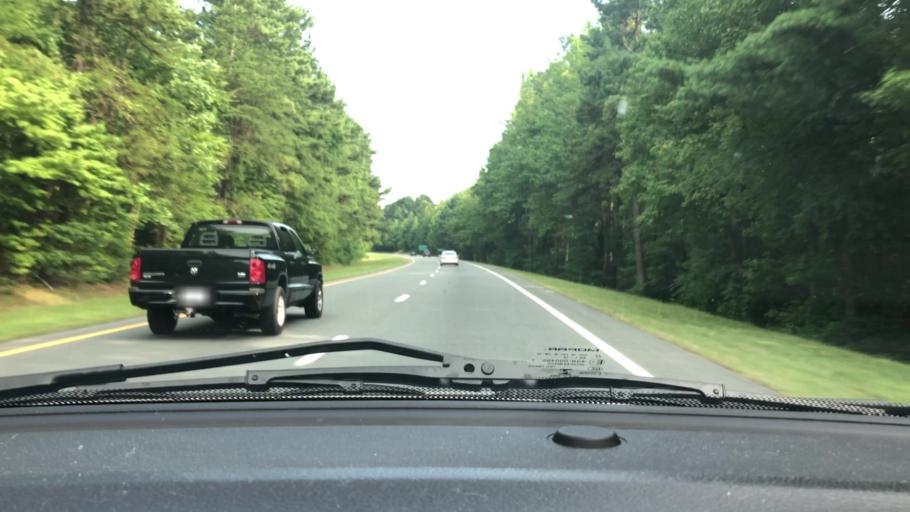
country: US
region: North Carolina
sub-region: Guilford County
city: Forest Oaks
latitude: 35.9078
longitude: -79.6723
